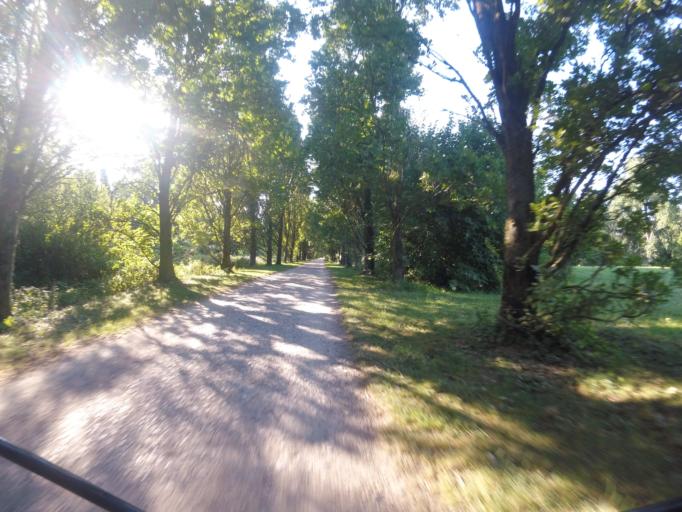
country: DE
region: Baden-Wuerttemberg
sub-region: Regierungsbezirk Stuttgart
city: Asperg
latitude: 48.9160
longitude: 9.1649
